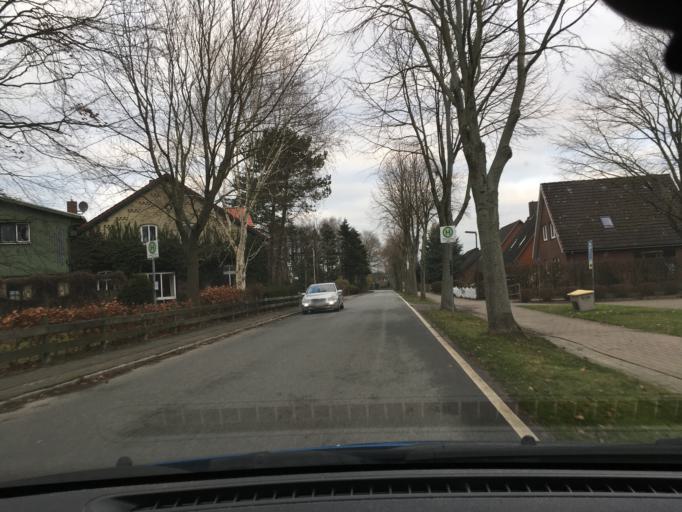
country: DE
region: Schleswig-Holstein
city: Lohe-Rickelshof
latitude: 54.1837
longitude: 9.0615
